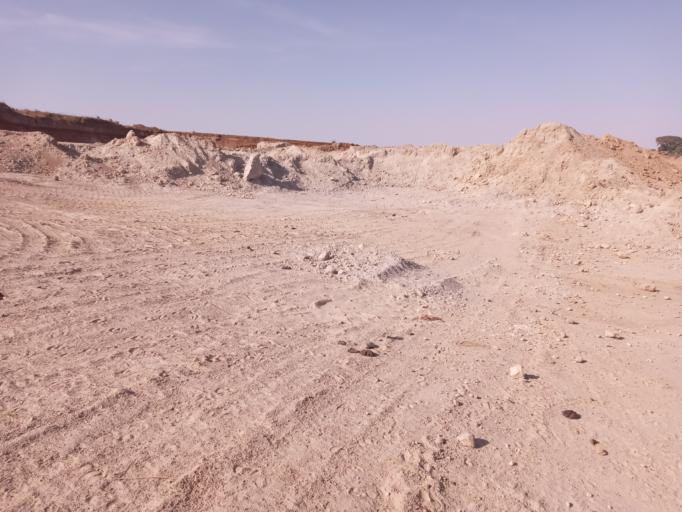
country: ET
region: Oromiya
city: Shashemene
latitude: 7.3157
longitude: 38.6261
